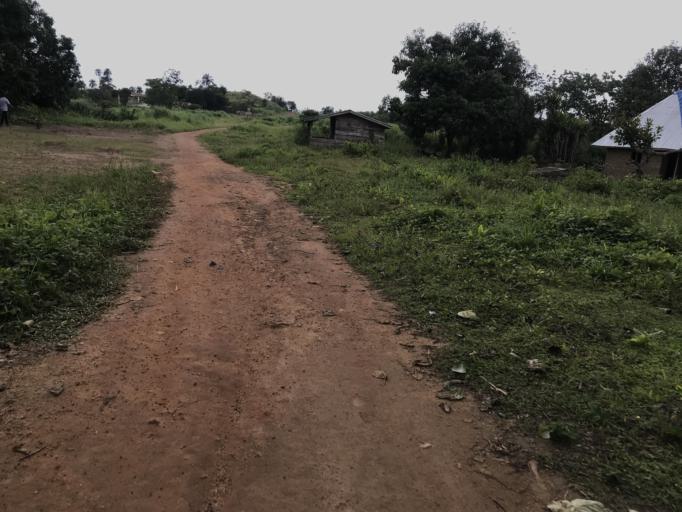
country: GN
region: Nzerekore
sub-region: Prefecture de Guekedou
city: Gueckedou
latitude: 8.4724
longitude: -10.2818
